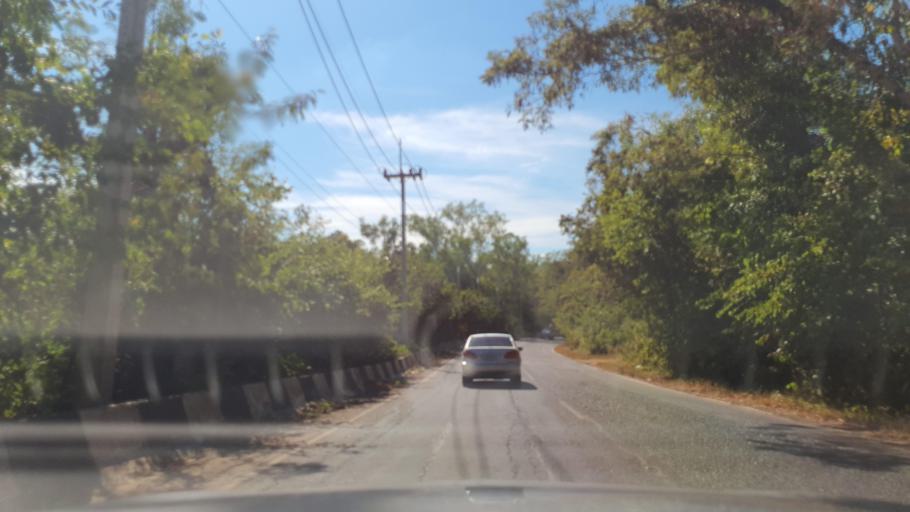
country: TH
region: Kalasin
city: Khao Wong
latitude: 16.7626
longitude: 104.1542
